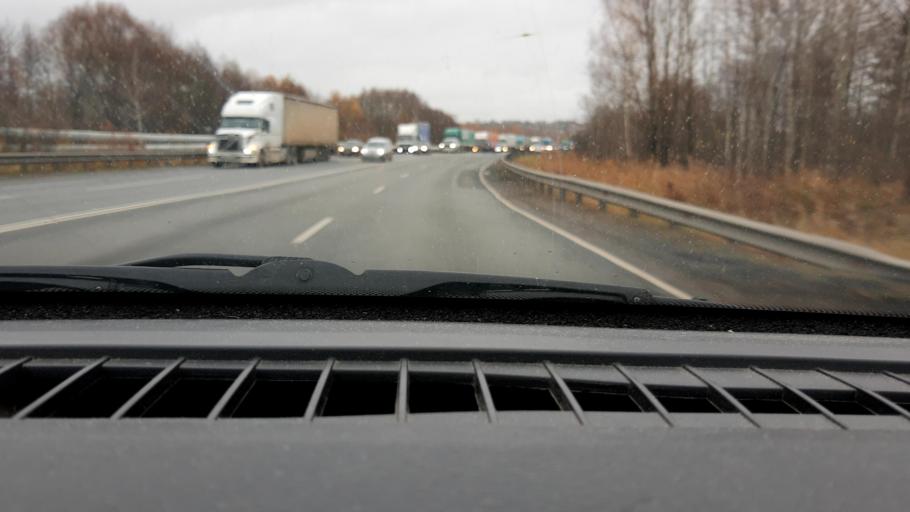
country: RU
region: Nizjnij Novgorod
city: Kstovo
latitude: 56.1213
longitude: 44.1567
